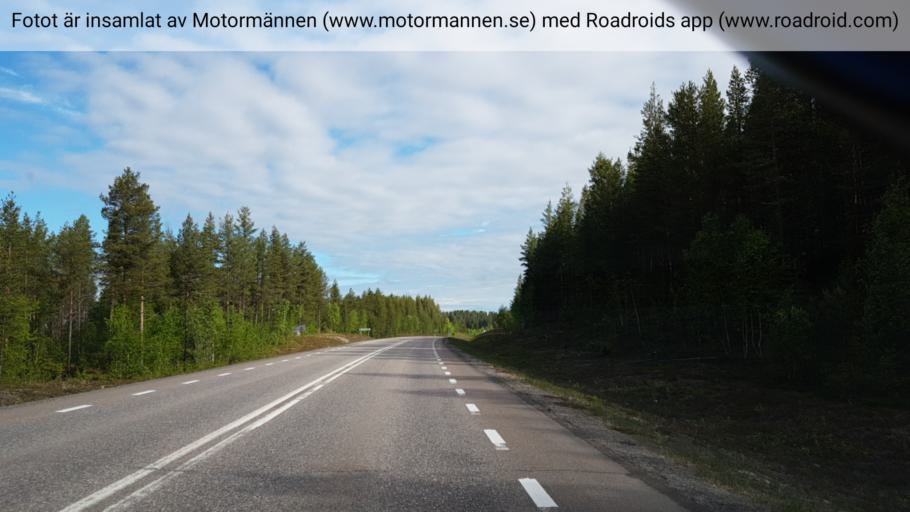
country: SE
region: Norrbotten
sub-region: Gallivare Kommun
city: Malmberget
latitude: 67.4822
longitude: 21.1245
